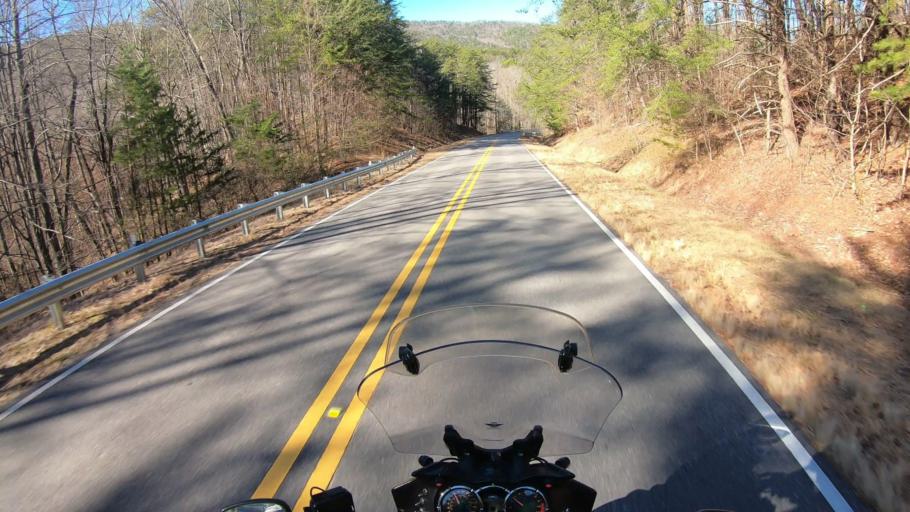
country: US
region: Alabama
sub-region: Calhoun County
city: Oxford
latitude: 33.4860
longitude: -85.7875
